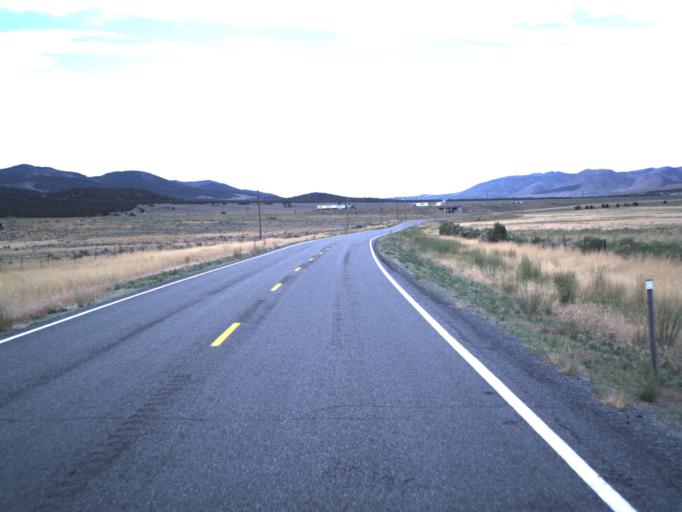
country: US
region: Utah
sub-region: Beaver County
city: Beaver
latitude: 38.5939
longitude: -112.5817
